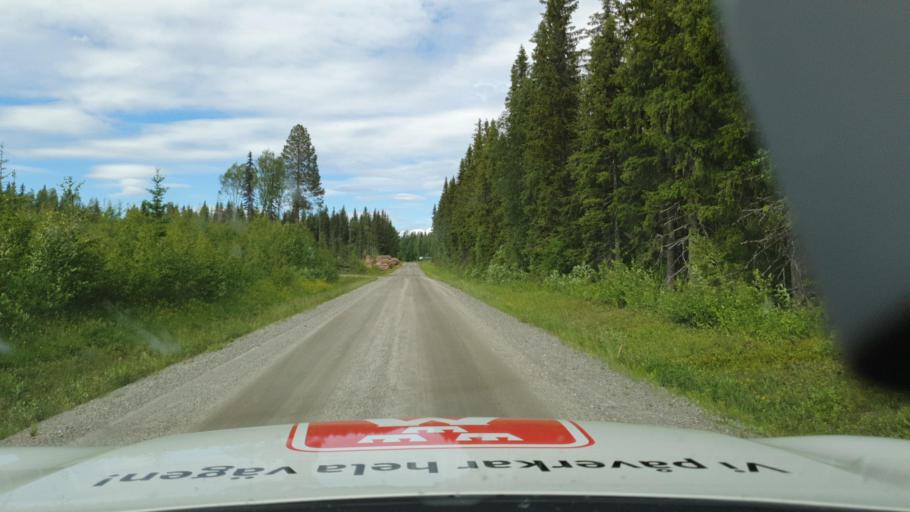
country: SE
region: Vaesterbotten
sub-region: Norsjo Kommun
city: Norsjoe
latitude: 64.7927
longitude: 19.6664
